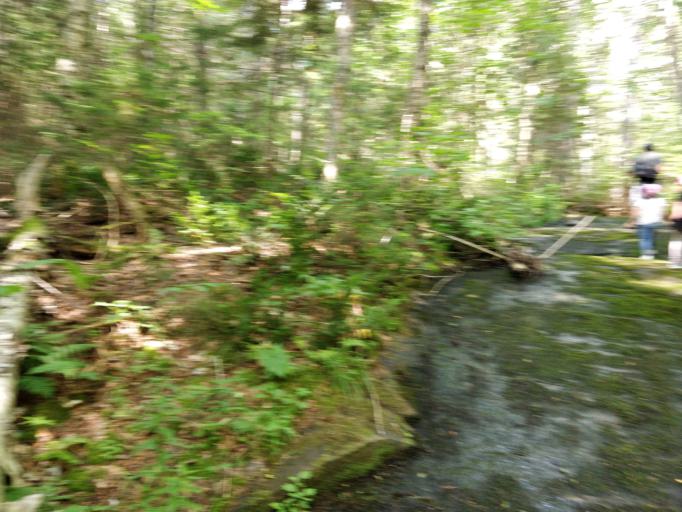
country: CA
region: Quebec
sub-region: Laurentides
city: Sainte-Agathe-des-Monts
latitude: 46.3446
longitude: -74.2735
